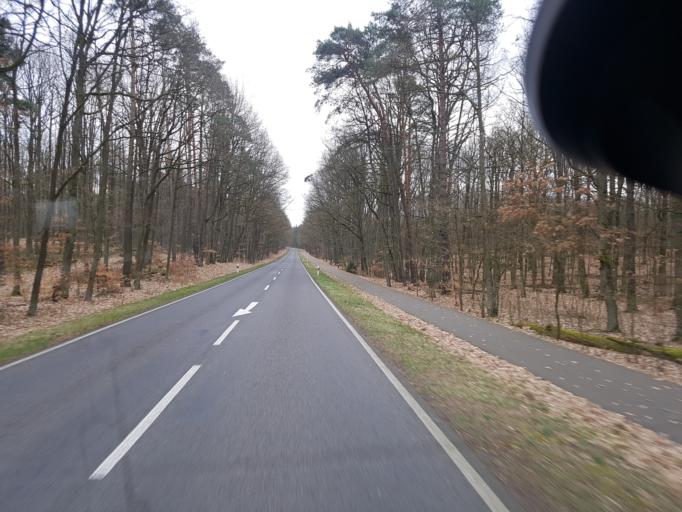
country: DE
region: Brandenburg
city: Gross Lindow
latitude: 52.1790
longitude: 14.4777
